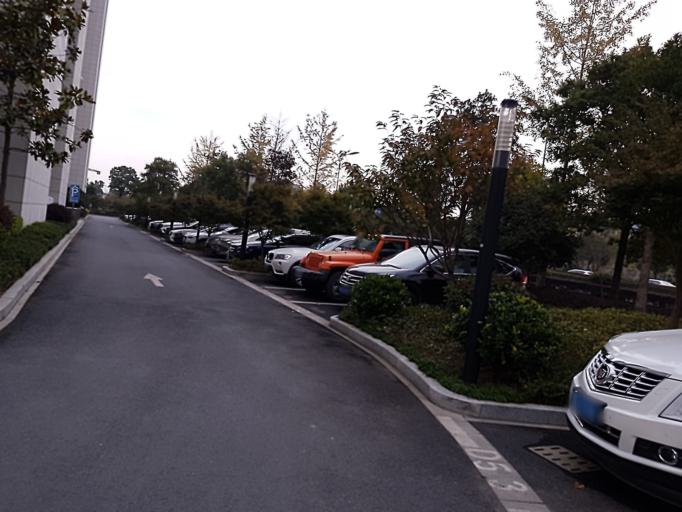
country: CN
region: Zhejiang Sheng
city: Cangqian
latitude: 30.2816
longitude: 120.0048
